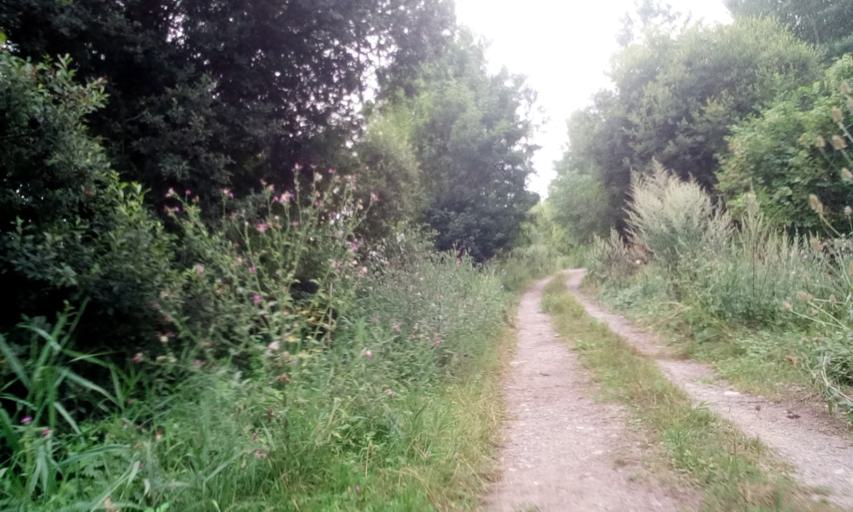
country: FR
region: Lower Normandy
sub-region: Departement du Calvados
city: Argences
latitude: 49.1446
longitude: -0.1834
